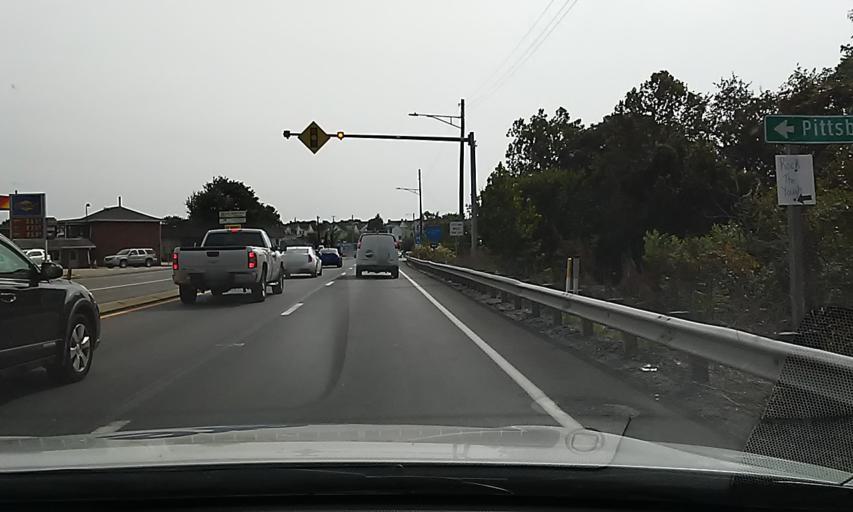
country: US
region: Pennsylvania
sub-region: Fayette County
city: Connellsville
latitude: 40.0262
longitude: -79.5897
